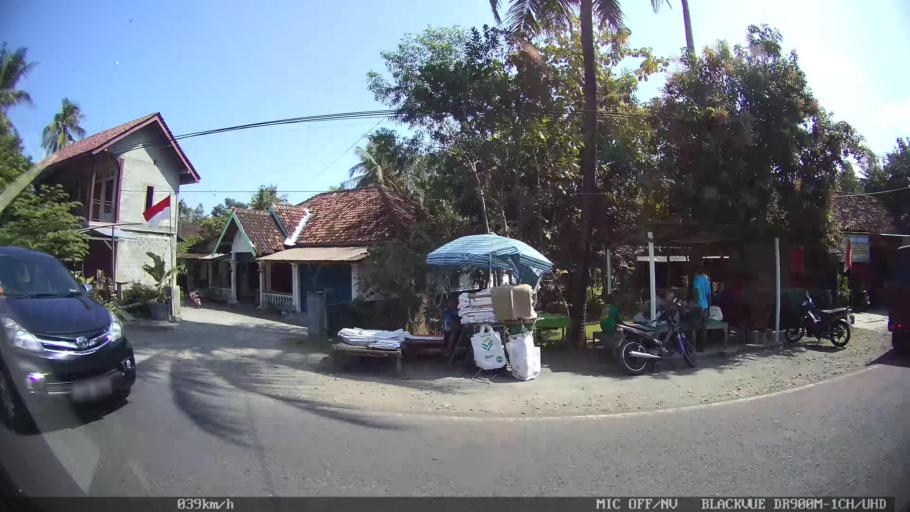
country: ID
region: Daerah Istimewa Yogyakarta
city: Srandakan
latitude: -7.9496
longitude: 110.2202
